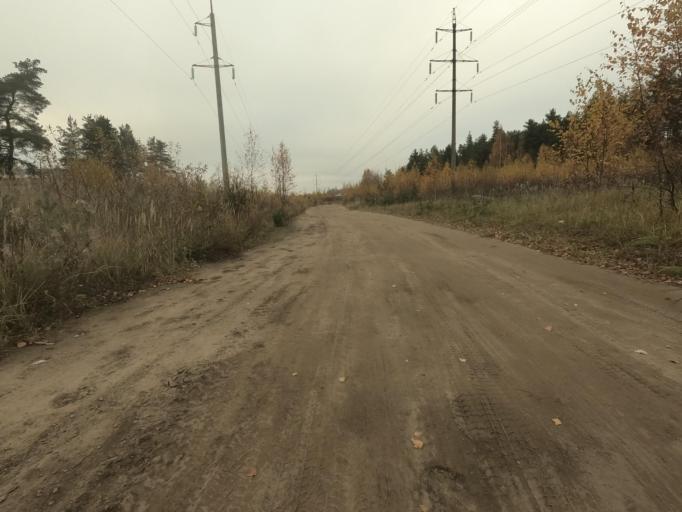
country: RU
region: Leningrad
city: Kirovsk
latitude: 59.8544
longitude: 30.9855
